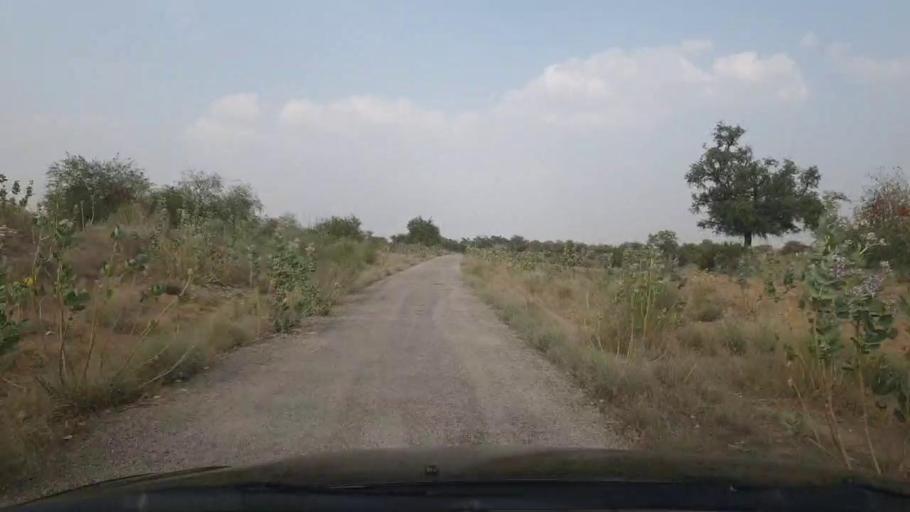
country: PK
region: Sindh
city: Islamkot
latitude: 25.0424
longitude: 70.5670
